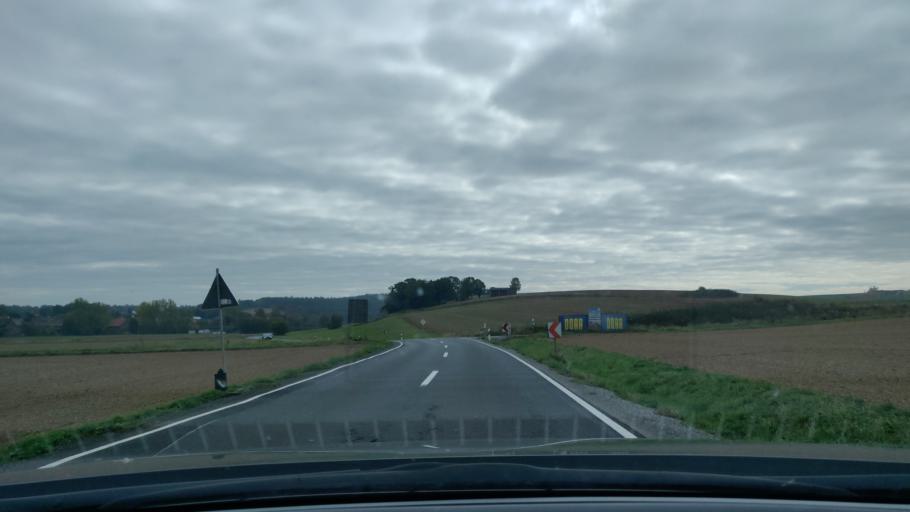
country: DE
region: Hesse
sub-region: Regierungsbezirk Kassel
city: Neuental
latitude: 51.0008
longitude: 9.2022
